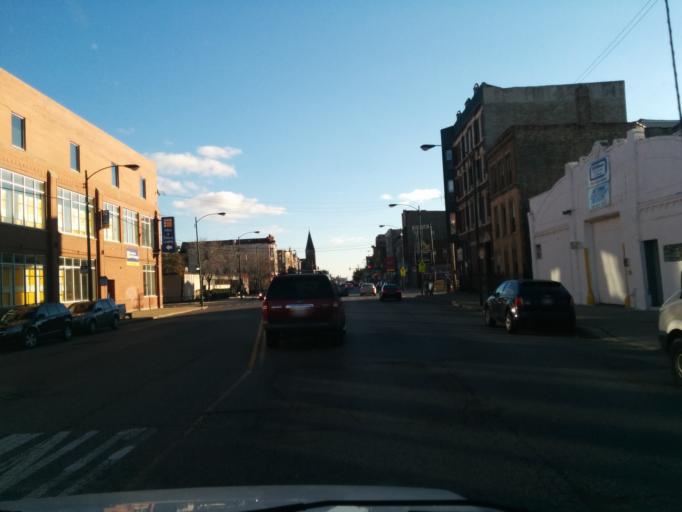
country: US
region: Illinois
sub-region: Cook County
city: Chicago
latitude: 41.8593
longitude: -87.6662
